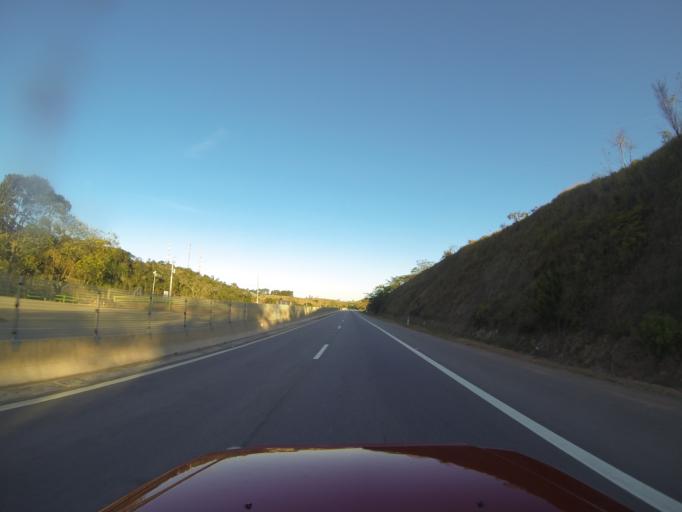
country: BR
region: Sao Paulo
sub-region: Santa Branca
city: Santa Branca
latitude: -23.4314
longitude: -45.6256
